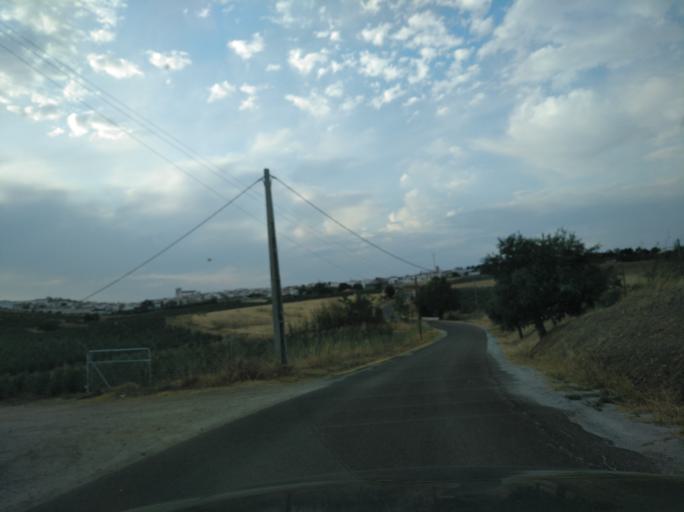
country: PT
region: Portalegre
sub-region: Campo Maior
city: Campo Maior
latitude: 39.0053
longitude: -7.0604
